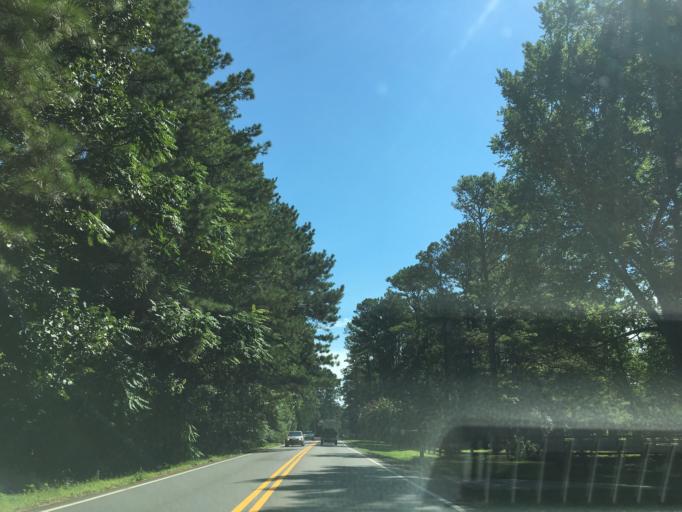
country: US
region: Georgia
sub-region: Fulton County
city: Milton
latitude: 34.1641
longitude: -84.2958
